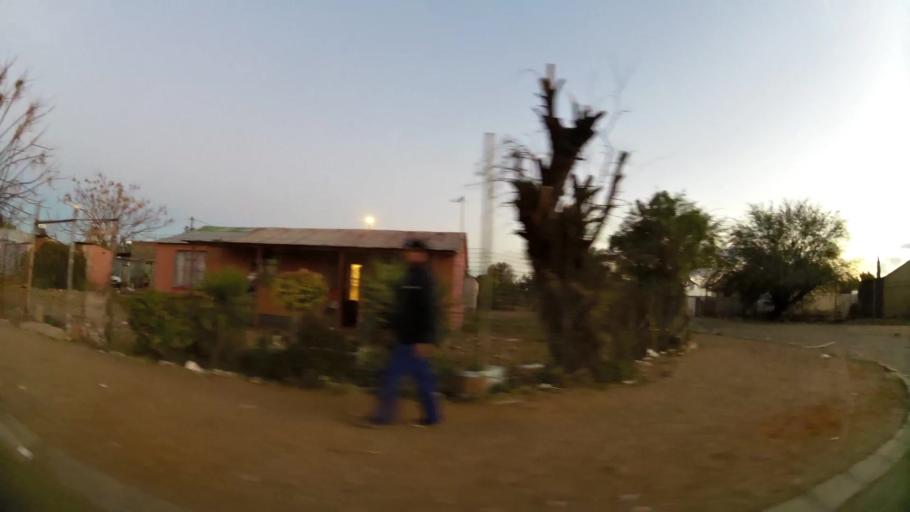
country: ZA
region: Northern Cape
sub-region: Frances Baard District Municipality
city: Kimberley
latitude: -28.7126
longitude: 24.7617
